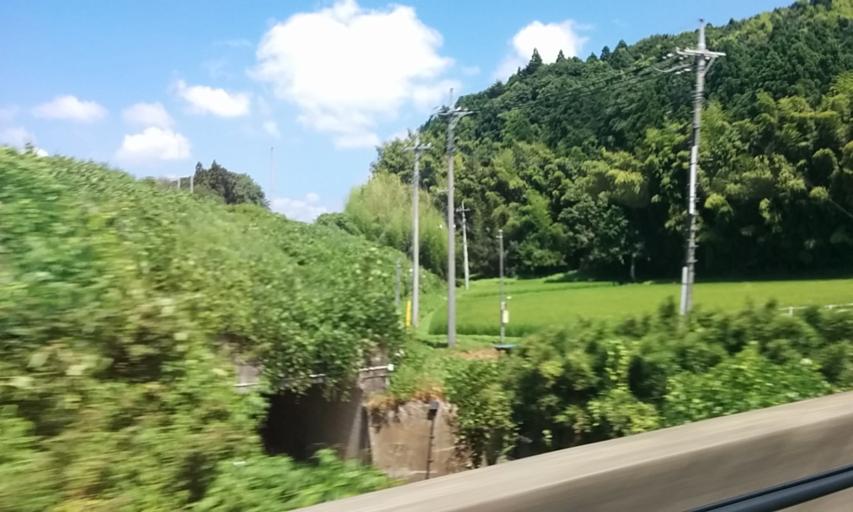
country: JP
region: Tochigi
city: Kuroiso
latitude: 36.9836
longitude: 140.0715
